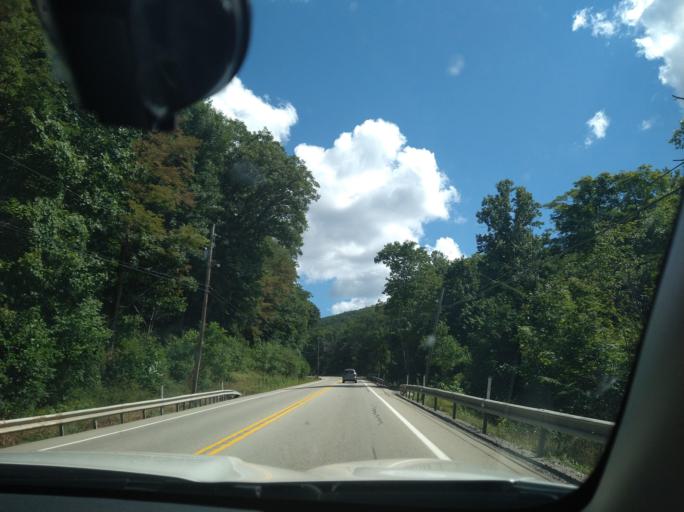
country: US
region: Pennsylvania
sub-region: Fayette County
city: Bear Rocks
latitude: 40.0757
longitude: -79.3133
